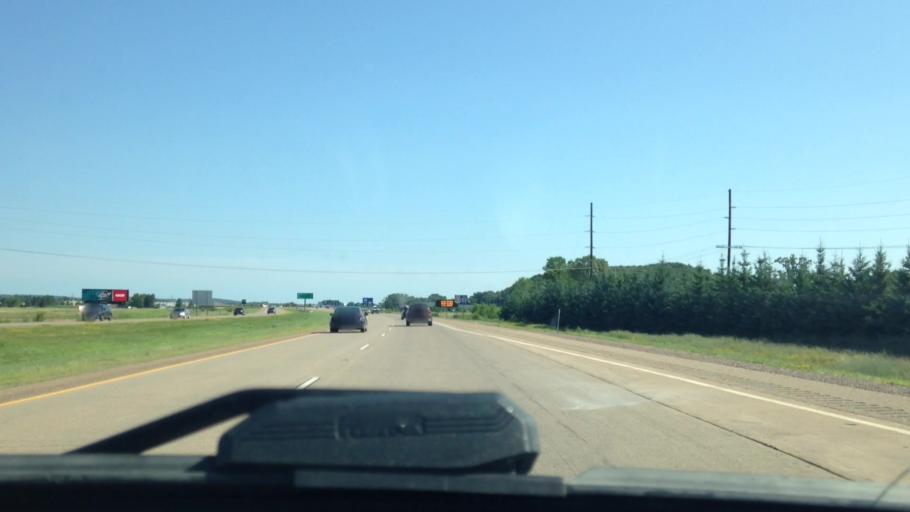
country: US
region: Wisconsin
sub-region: Chippewa County
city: Lake Hallie
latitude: 44.8665
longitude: -91.4232
